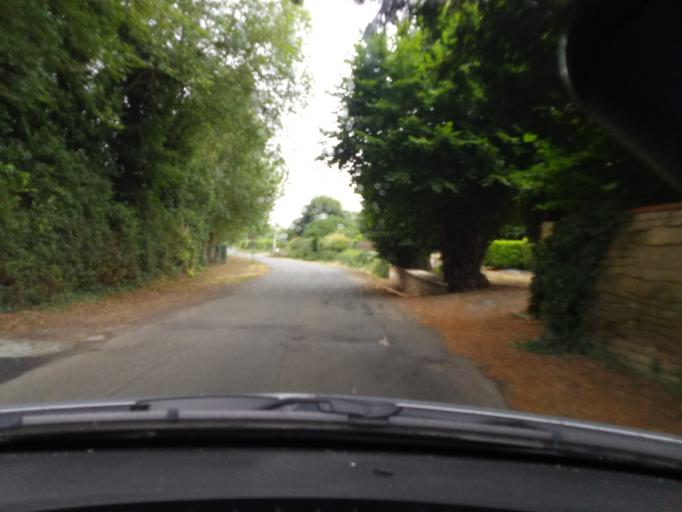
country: FR
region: Pays de la Loire
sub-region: Departement de la Vendee
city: Sainte-Gemme-la-Plaine
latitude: 46.4845
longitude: -1.1183
